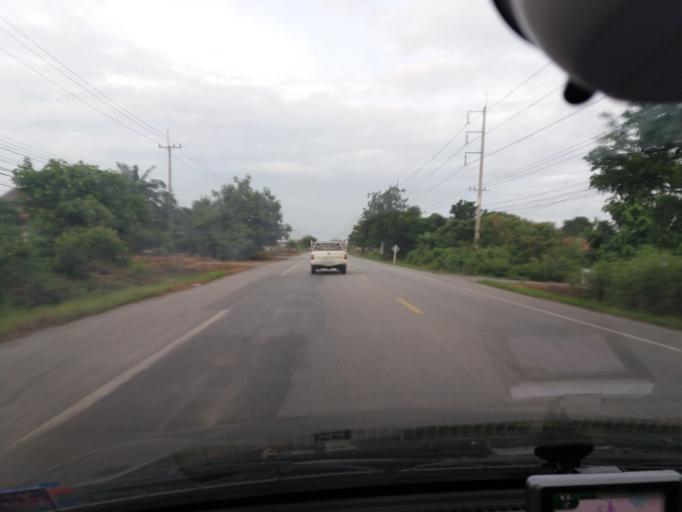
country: TH
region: Suphan Buri
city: U Thong
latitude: 14.4163
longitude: 99.9040
